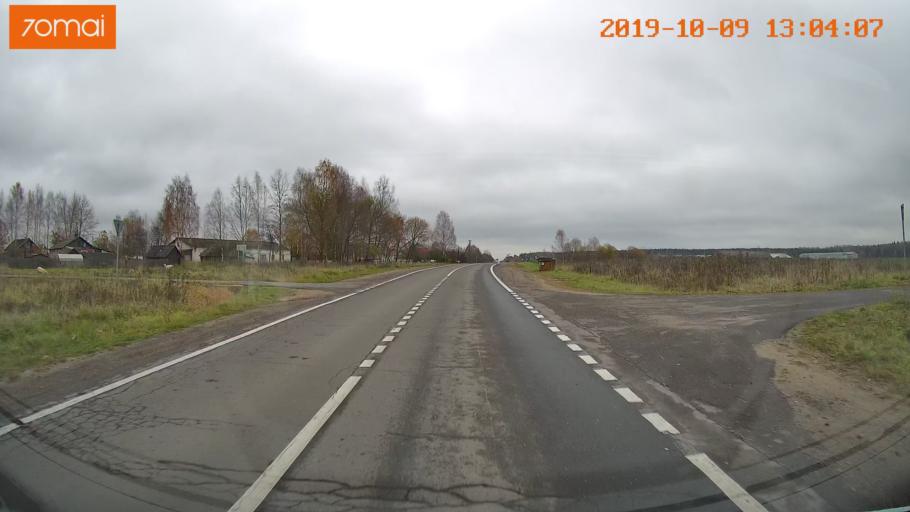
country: RU
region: Jaroslavl
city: Lyubim
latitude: 58.3588
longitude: 40.5463
